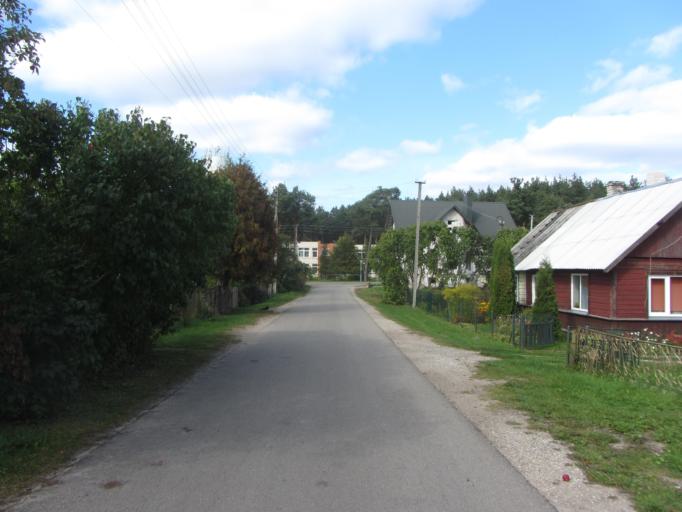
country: LT
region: Vilnius County
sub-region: Trakai
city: Rudiskes
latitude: 54.5139
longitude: 24.8233
